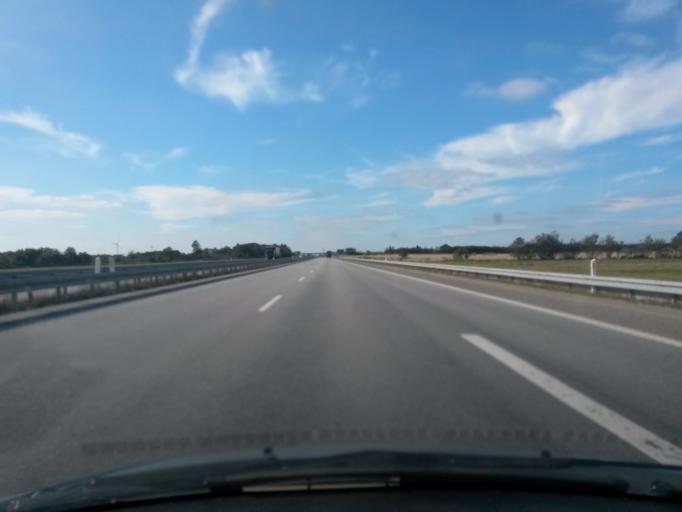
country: DK
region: Central Jutland
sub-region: Ikast-Brande Kommune
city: Bording Kirkeby
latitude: 56.1307
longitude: 9.3424
